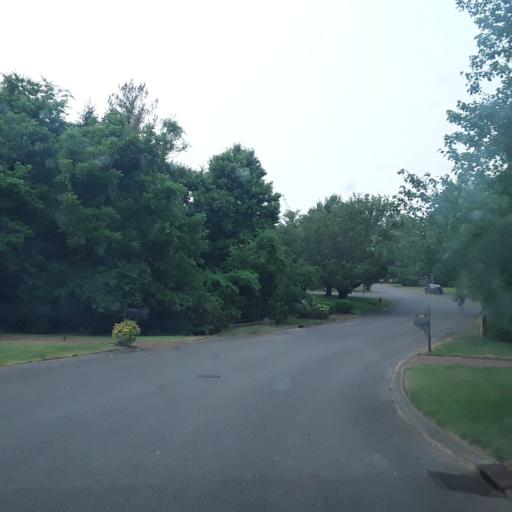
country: US
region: Tennessee
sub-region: Williamson County
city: Brentwood
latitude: 36.0466
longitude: -86.7724
